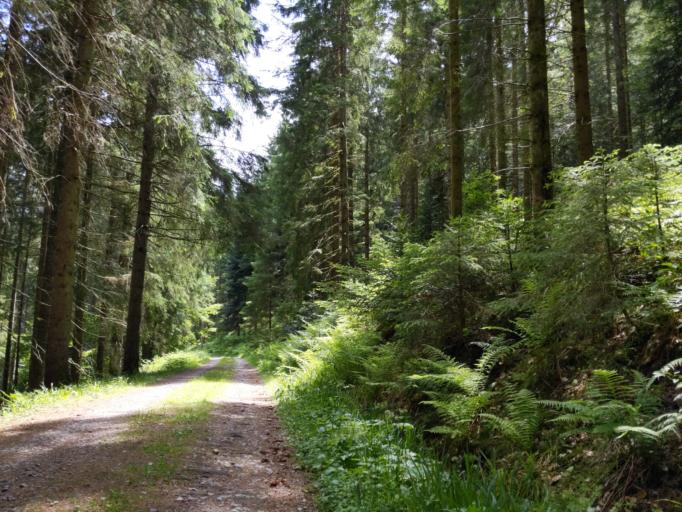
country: DE
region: Baden-Wuerttemberg
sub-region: Karlsruhe Region
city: Freudenstadt
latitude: 48.4356
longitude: 8.3723
